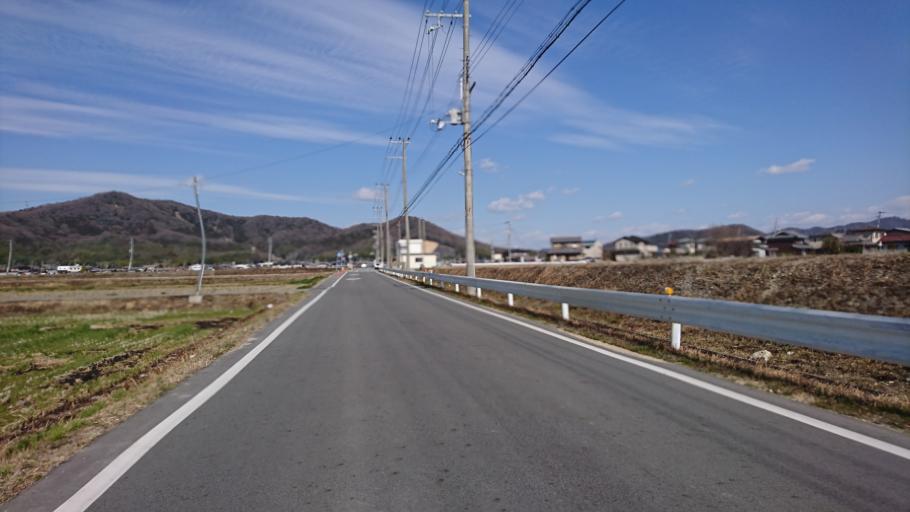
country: JP
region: Hyogo
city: Kakogawacho-honmachi
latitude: 34.8175
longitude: 134.8058
